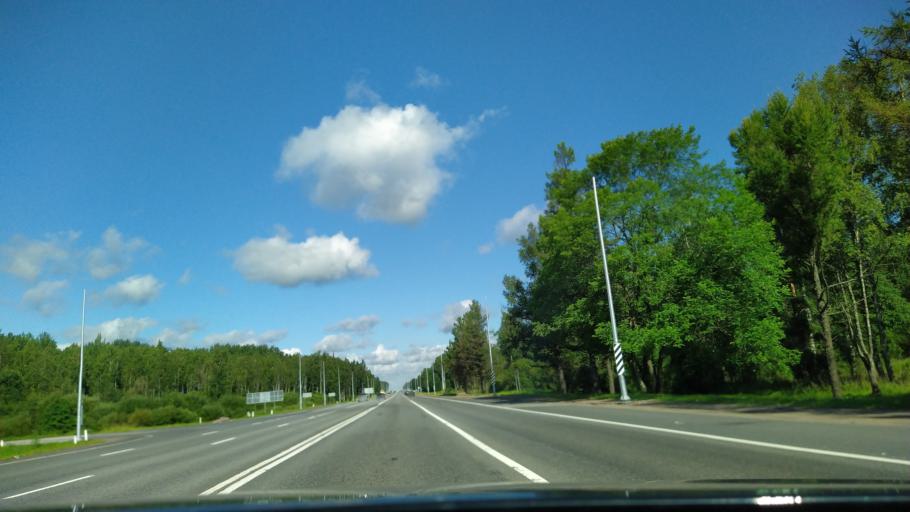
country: RU
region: Leningrad
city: Ul'yanovka
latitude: 59.5838
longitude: 30.7994
